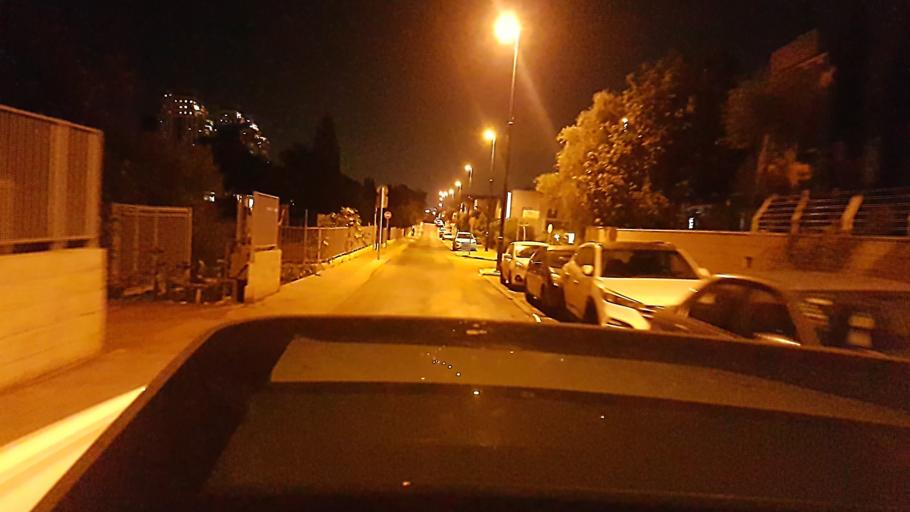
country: IL
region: Central District
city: Hod HaSharon
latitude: 32.1661
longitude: 34.8914
